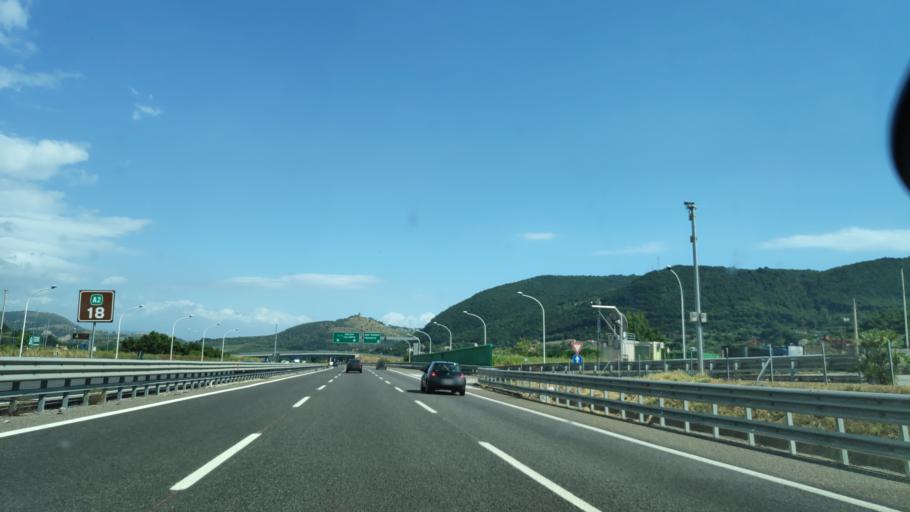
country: IT
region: Campania
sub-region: Provincia di Salerno
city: San Mango Piemonte
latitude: 40.6926
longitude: 14.8350
